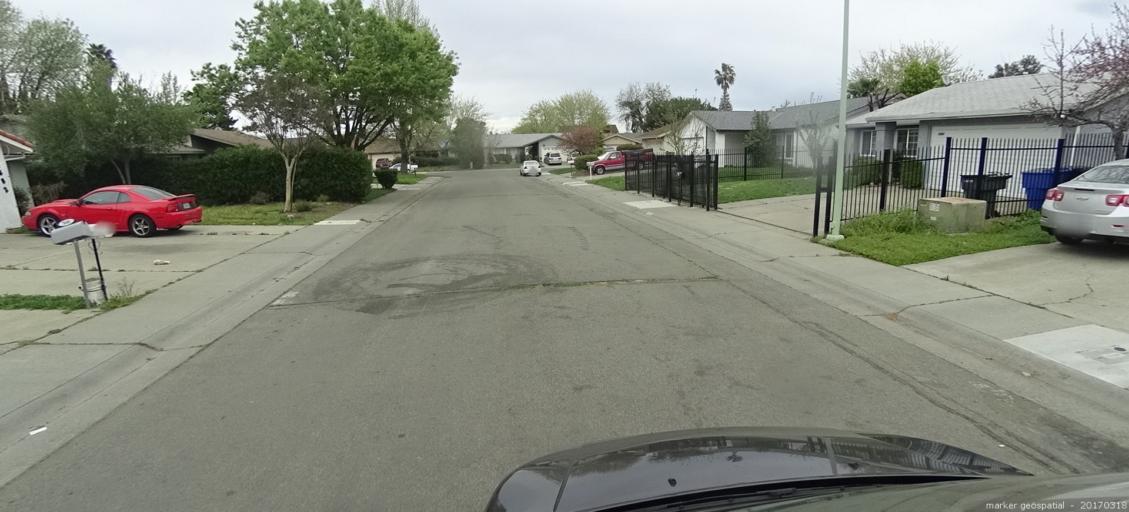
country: US
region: California
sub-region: Sacramento County
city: Florin
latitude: 38.4786
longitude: -121.4336
